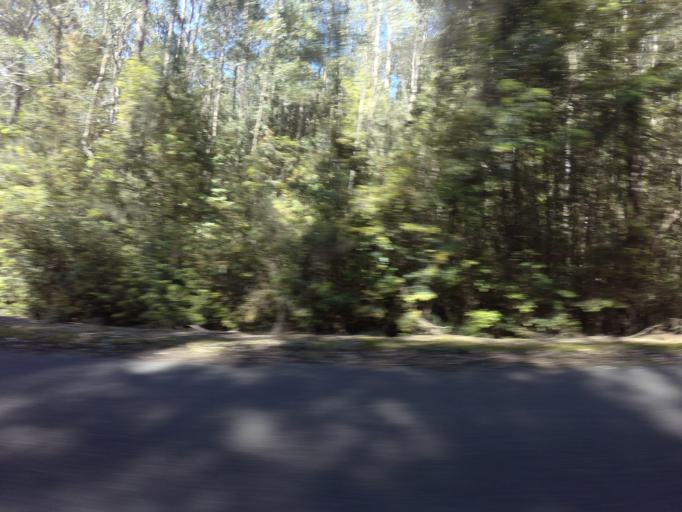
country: AU
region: Tasmania
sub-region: Huon Valley
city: Geeveston
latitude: -42.8220
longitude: 146.3333
